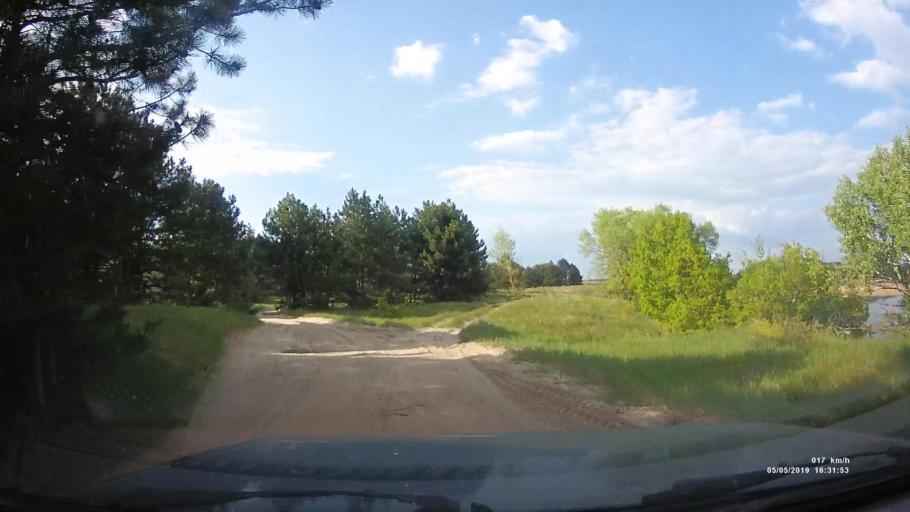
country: RU
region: Rostov
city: Ust'-Donetskiy
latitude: 47.7774
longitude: 41.0143
